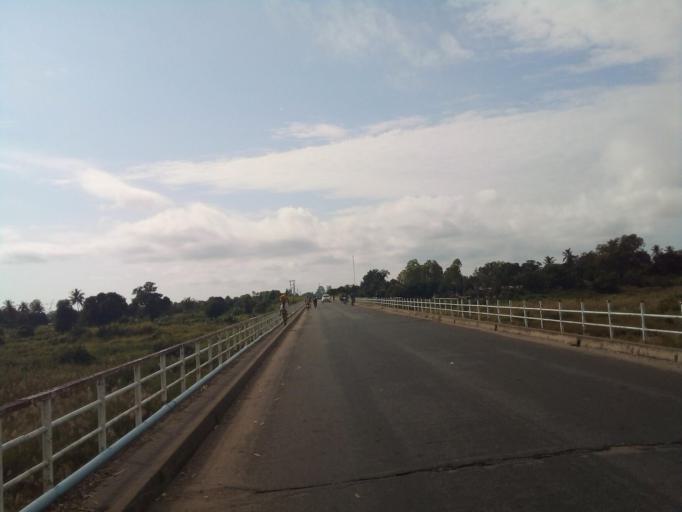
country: MZ
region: Zambezia
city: Quelimane
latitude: -17.5779
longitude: 36.6908
